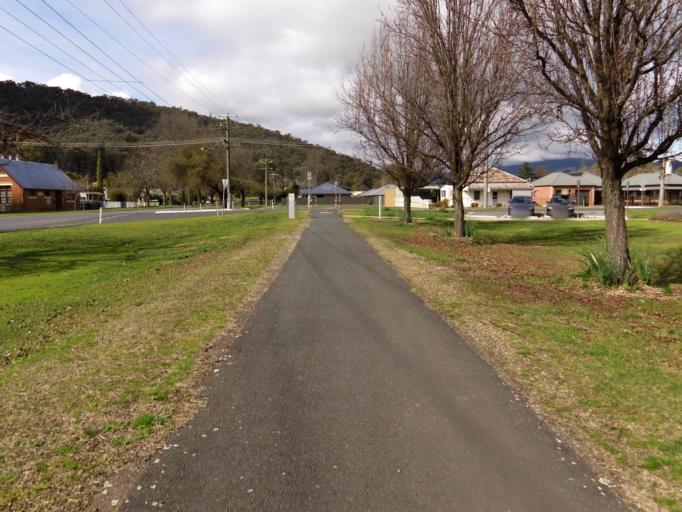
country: AU
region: Victoria
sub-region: Wangaratta
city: Wangaratta
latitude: -36.5621
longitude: 146.7281
